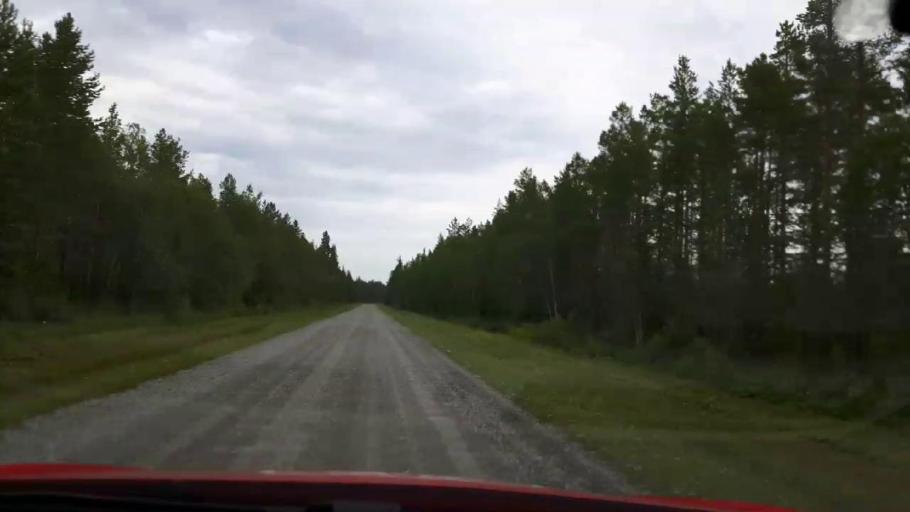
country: SE
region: Jaemtland
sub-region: Stroemsunds Kommun
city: Stroemsund
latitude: 63.7348
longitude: 15.5563
